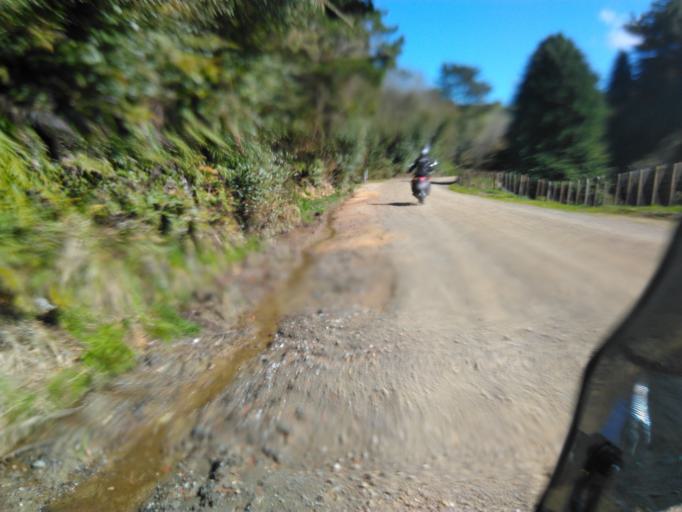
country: NZ
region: Bay of Plenty
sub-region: Opotiki District
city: Opotiki
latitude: -38.3325
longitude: 177.5769
